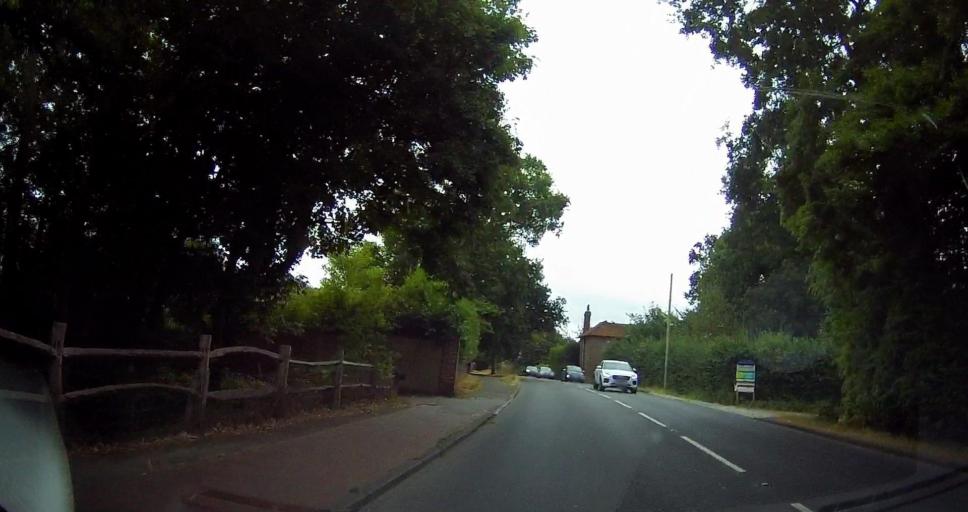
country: GB
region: England
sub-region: East Sussex
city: Wadhurst
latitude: 51.0645
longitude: 0.3343
